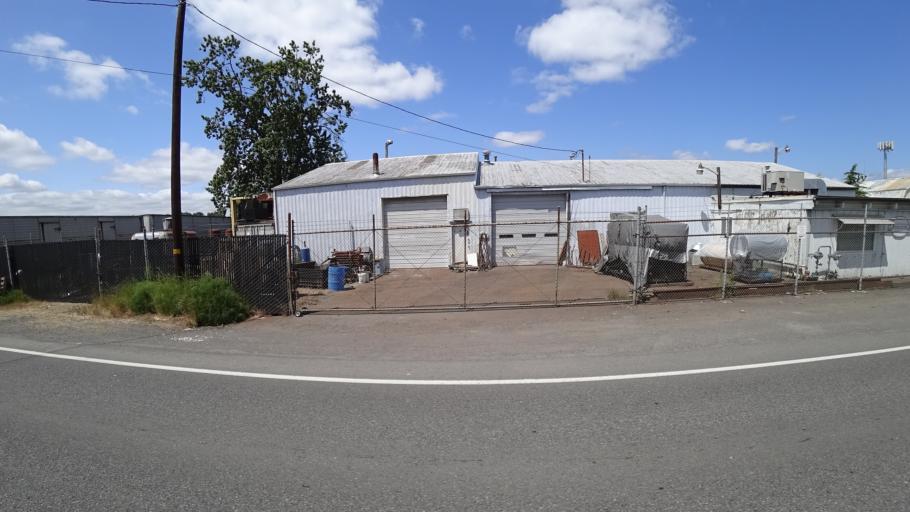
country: US
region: Washington
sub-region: Clark County
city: Vancouver
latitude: 45.5950
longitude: -122.6630
